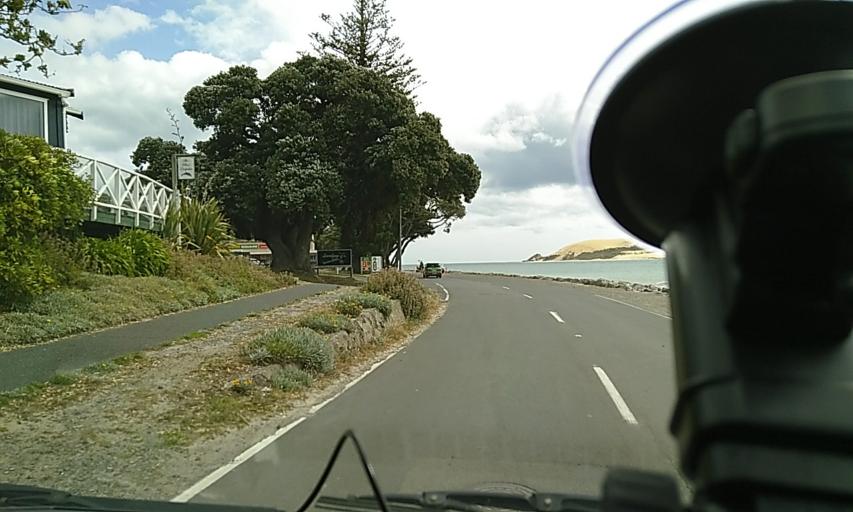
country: NZ
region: Northland
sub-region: Far North District
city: Ahipara
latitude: -35.5047
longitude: 173.3913
